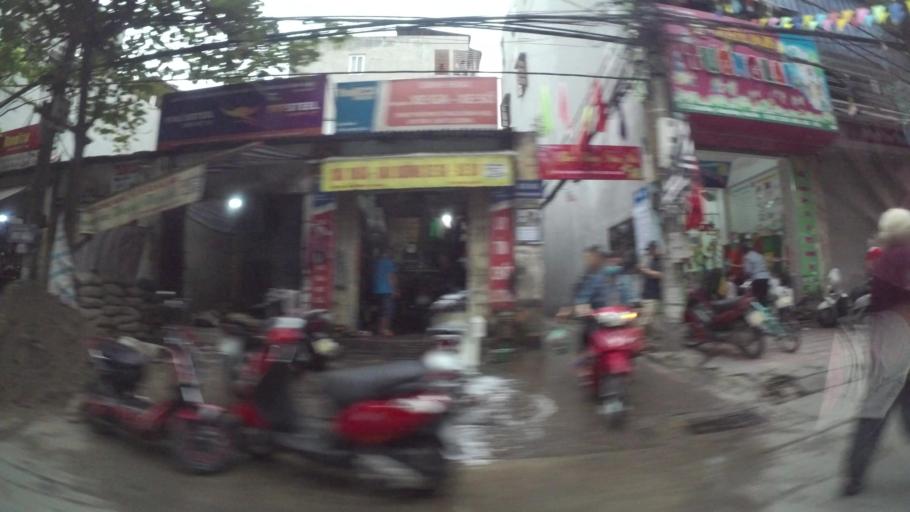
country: VN
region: Ha Noi
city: Hoan Kiem
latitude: 21.0207
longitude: 105.8631
